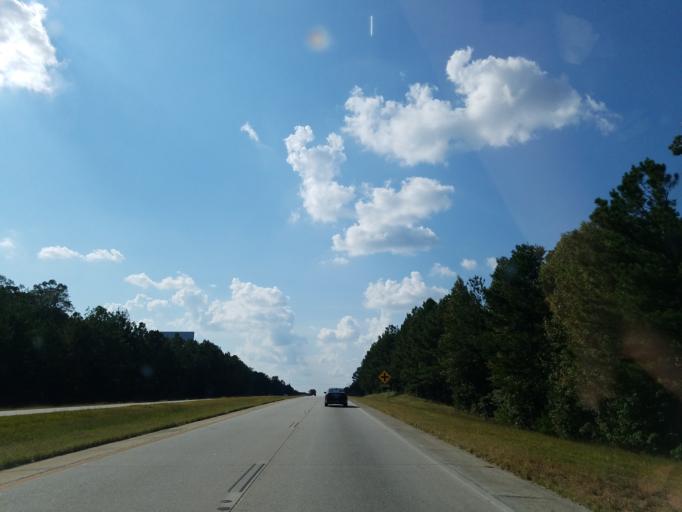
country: US
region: Georgia
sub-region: Oconee County
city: Bogart
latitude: 33.9430
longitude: -83.5648
